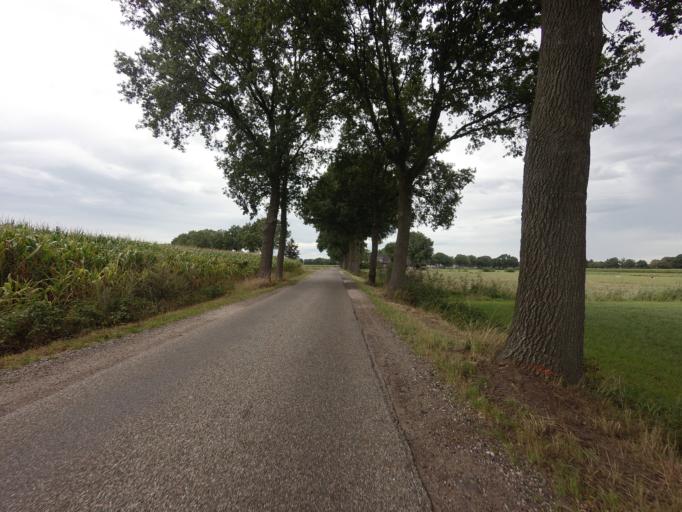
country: NL
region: Overijssel
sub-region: Gemeente Raalte
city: Raalte
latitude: 52.3619
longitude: 6.3535
